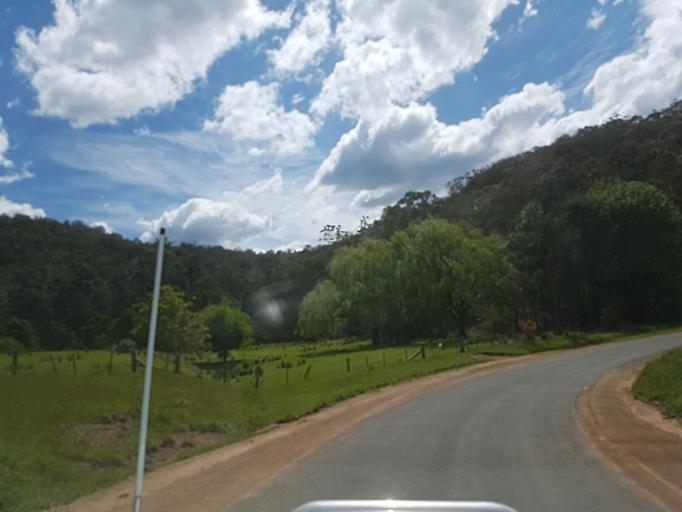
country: AU
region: Victoria
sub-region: East Gippsland
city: Bairnsdale
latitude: -37.4258
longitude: 147.2501
